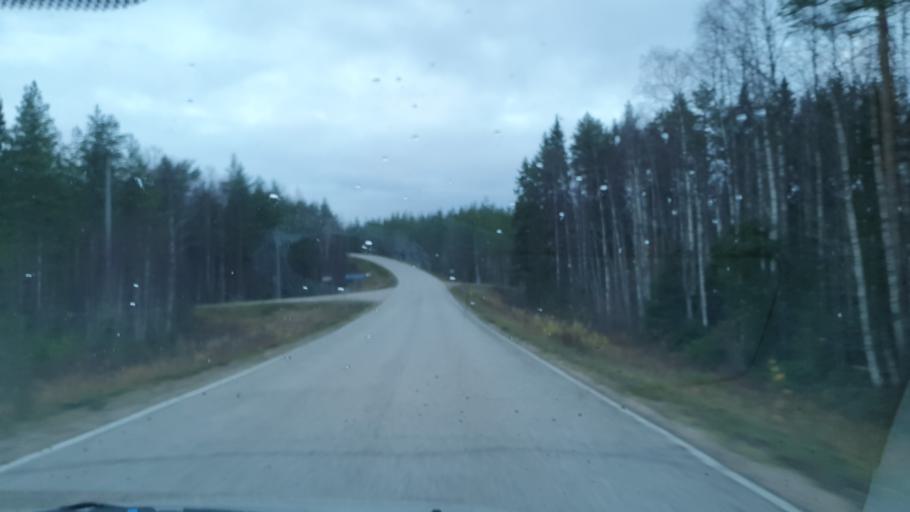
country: FI
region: Kainuu
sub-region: Kajaani
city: Ristijaervi
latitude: 64.4376
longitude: 28.3689
